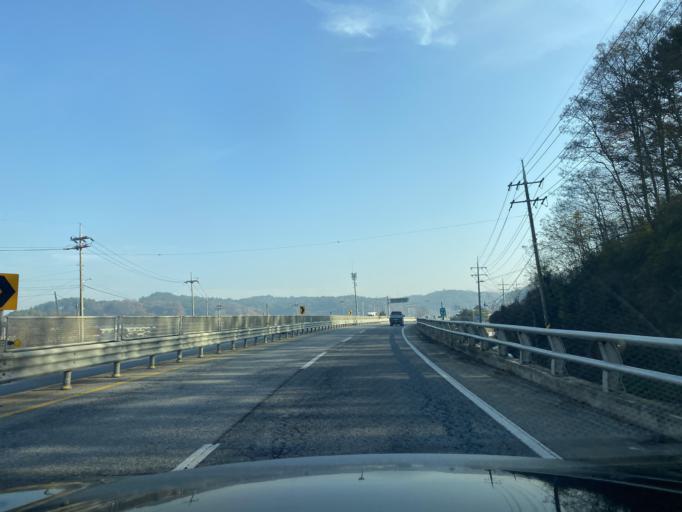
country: KR
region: Chungcheongnam-do
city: Yesan
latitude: 36.7457
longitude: 126.8631
